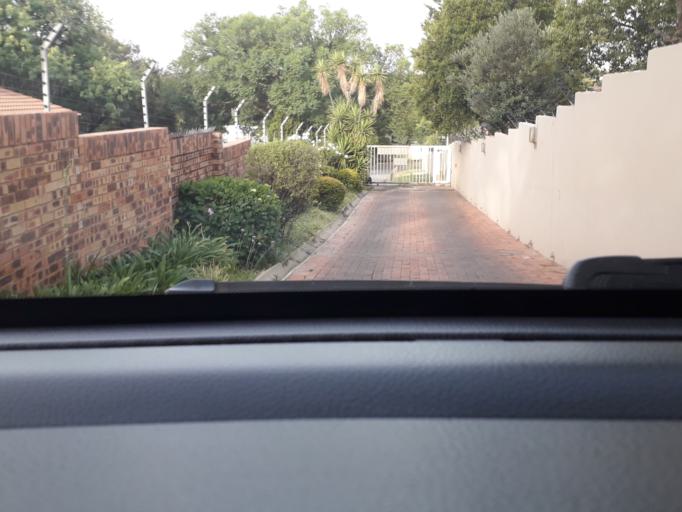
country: ZA
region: Gauteng
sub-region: City of Johannesburg Metropolitan Municipality
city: Midrand
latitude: -26.0686
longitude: 28.0634
